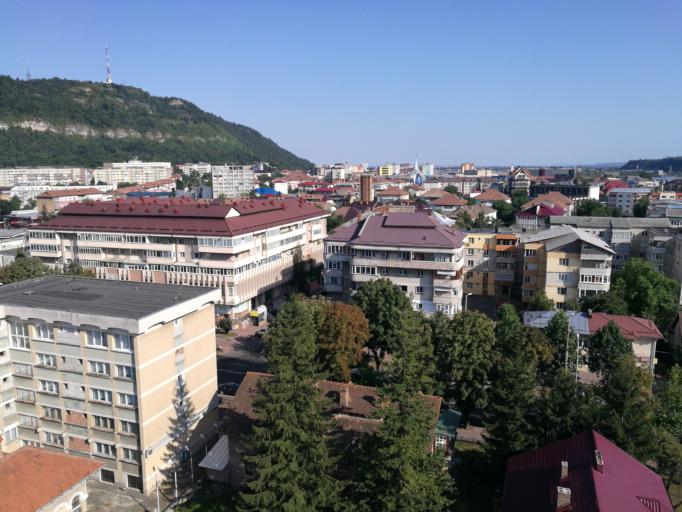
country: RO
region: Neamt
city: Piatra Neamt
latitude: 46.9292
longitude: 26.3621
